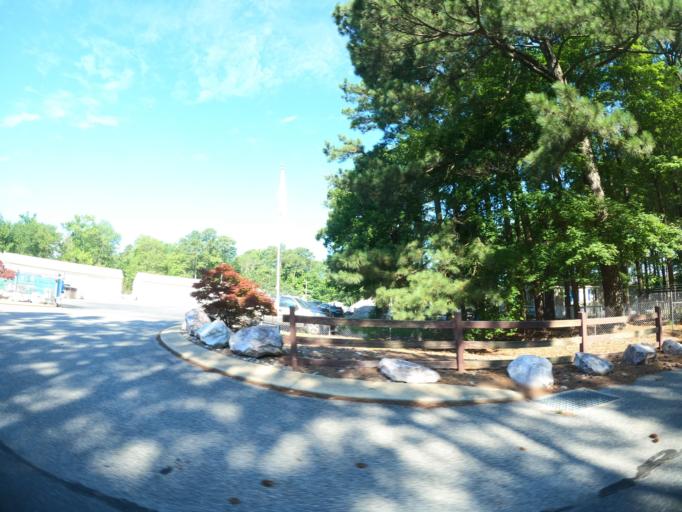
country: US
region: Delaware
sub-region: Sussex County
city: Ocean View
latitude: 38.5188
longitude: -75.0980
